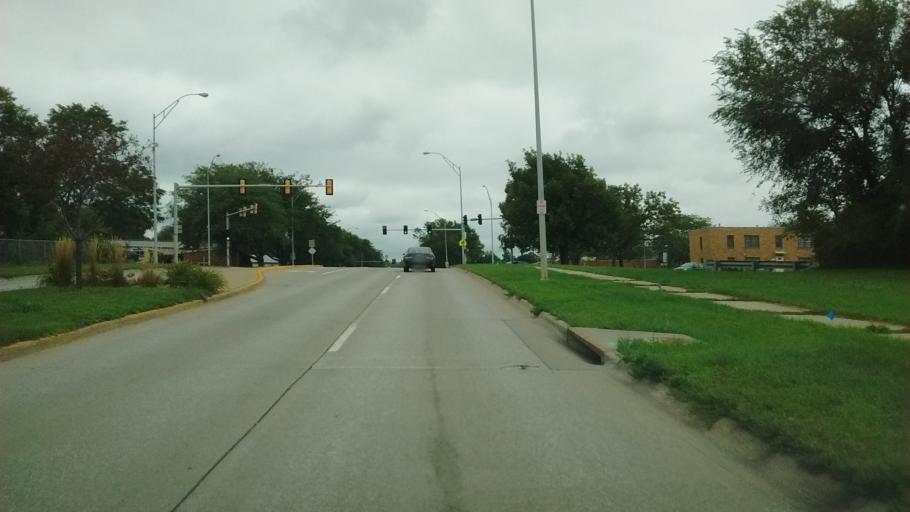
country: US
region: Iowa
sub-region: Woodbury County
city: Sioux City
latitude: 42.4986
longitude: -96.4218
